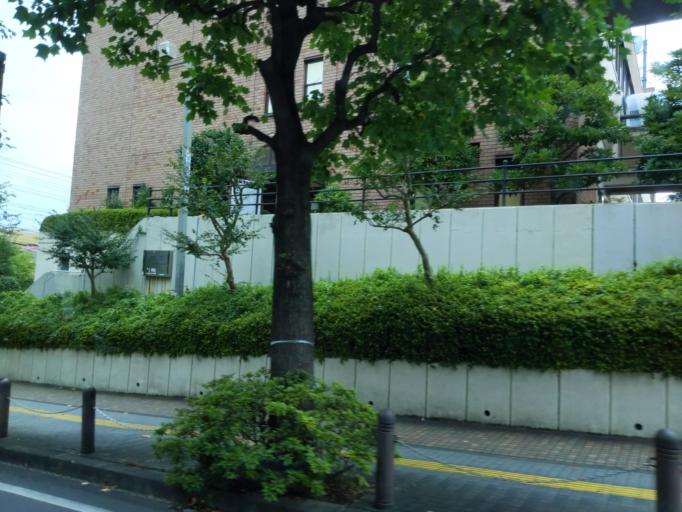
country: JP
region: Tokyo
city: Chofugaoka
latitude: 35.5890
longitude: 139.5783
